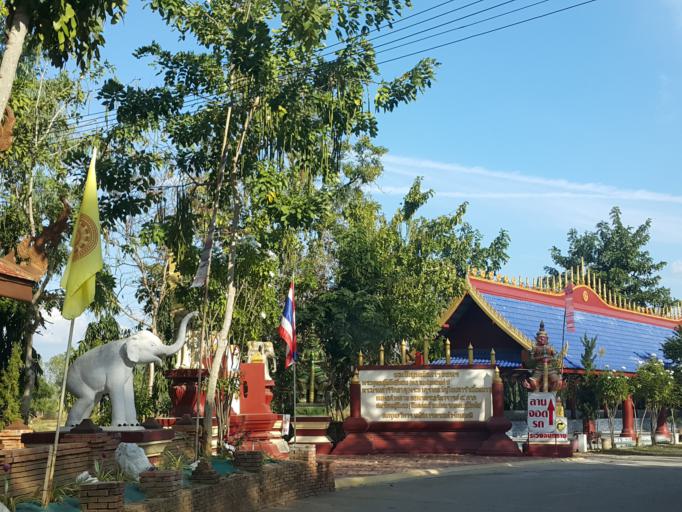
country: TH
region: Sukhothai
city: Thung Saliam
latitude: 17.3237
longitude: 99.5512
